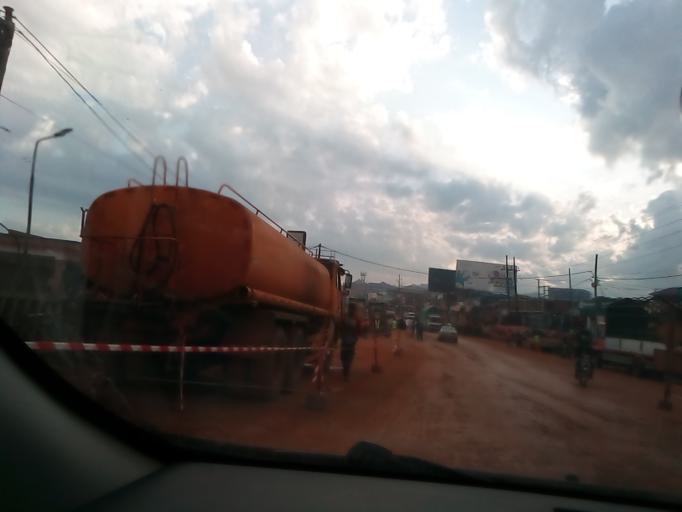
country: UG
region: Central Region
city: Masaka
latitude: -0.3191
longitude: 31.7586
